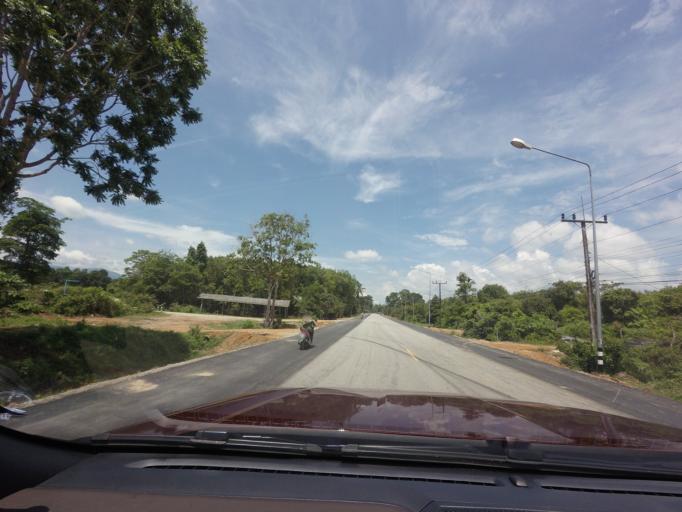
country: TH
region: Narathiwat
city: Ra-ngae
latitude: 6.2803
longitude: 101.7003
